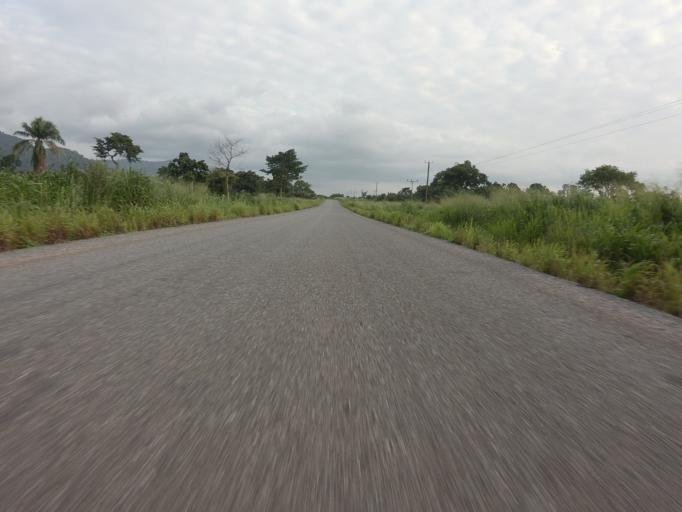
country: GH
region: Volta
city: Kpandu
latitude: 6.8590
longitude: 0.3957
